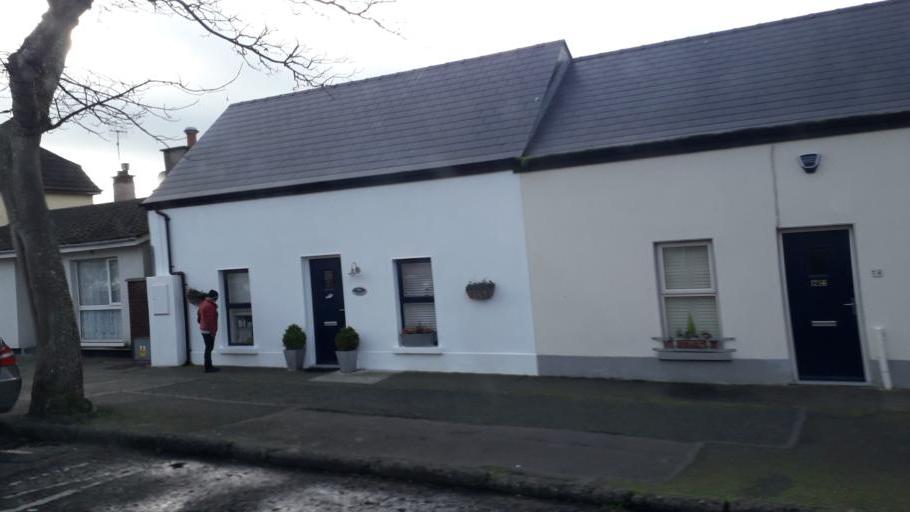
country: IE
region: Leinster
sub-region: Fingal County
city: Skerries
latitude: 53.5779
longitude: -6.1059
